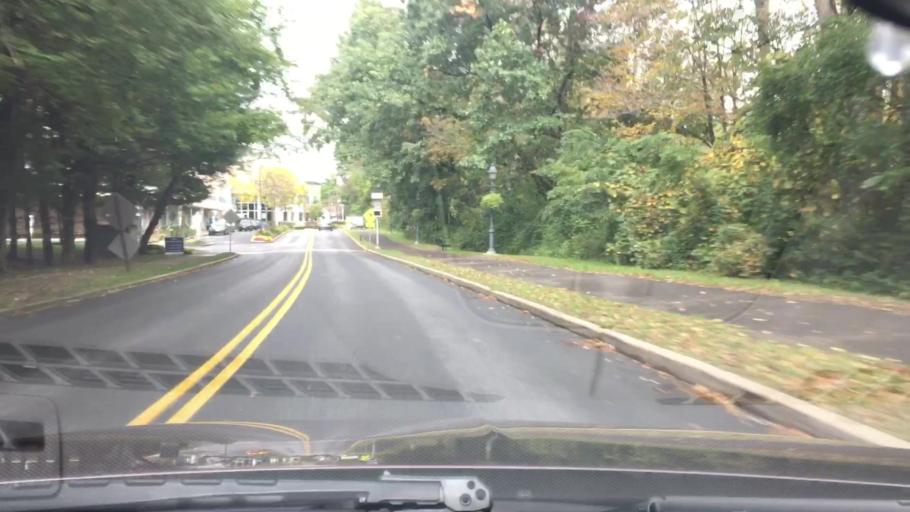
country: US
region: Connecticut
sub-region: Fairfield County
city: Wilton
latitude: 41.1888
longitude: -73.4300
